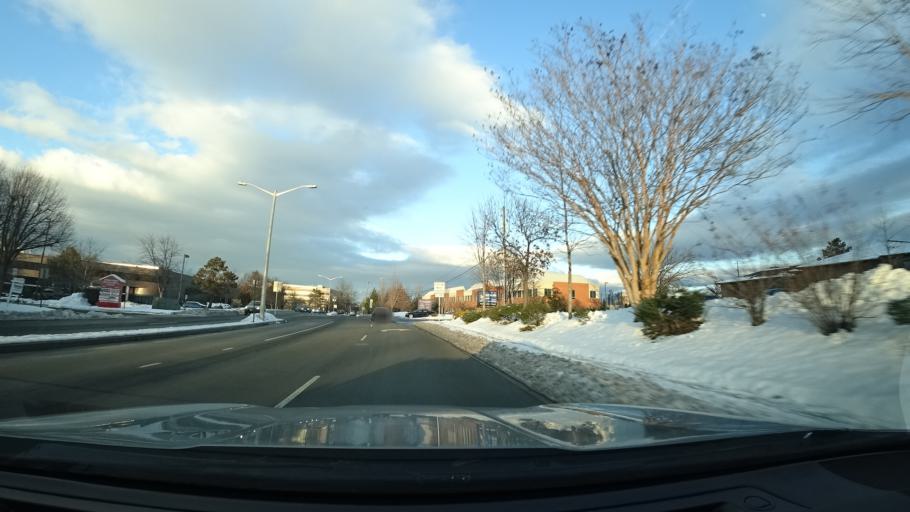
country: US
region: Virginia
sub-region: Fairfax County
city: Herndon
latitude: 38.9570
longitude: -77.3762
